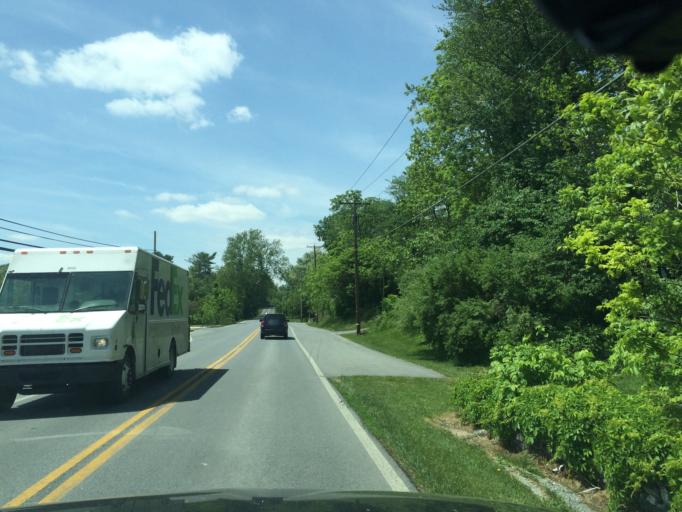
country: US
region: Maryland
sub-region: Carroll County
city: Westminster
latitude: 39.5524
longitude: -76.9585
